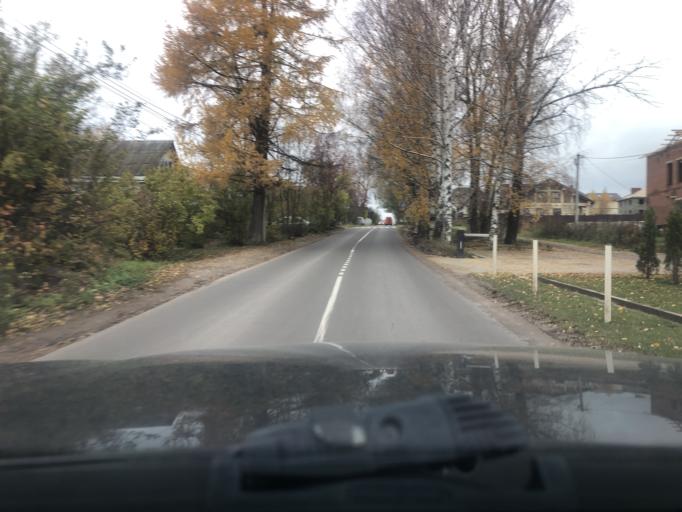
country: RU
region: Moskovskaya
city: Sergiyev Posad
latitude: 56.3006
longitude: 38.1106
